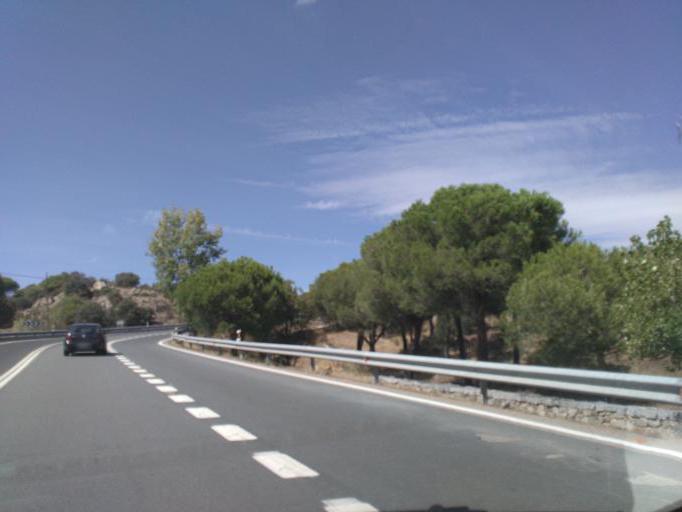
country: ES
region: Madrid
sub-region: Provincia de Madrid
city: Torrelodones
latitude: 40.5533
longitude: -3.9602
